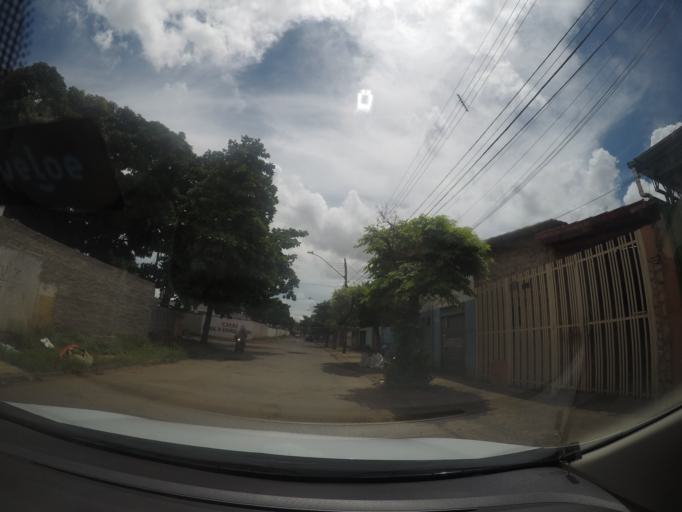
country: BR
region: Goias
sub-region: Goiania
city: Goiania
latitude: -16.6725
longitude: -49.3080
